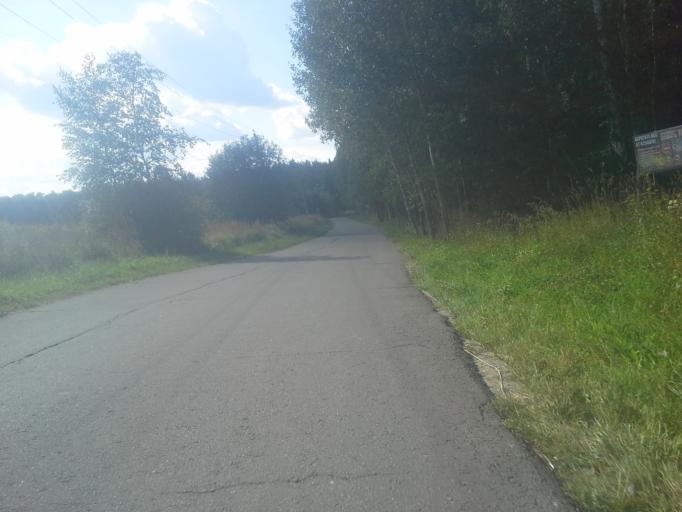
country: RU
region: Moskovskaya
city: Kievskij
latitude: 55.3288
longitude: 37.0104
